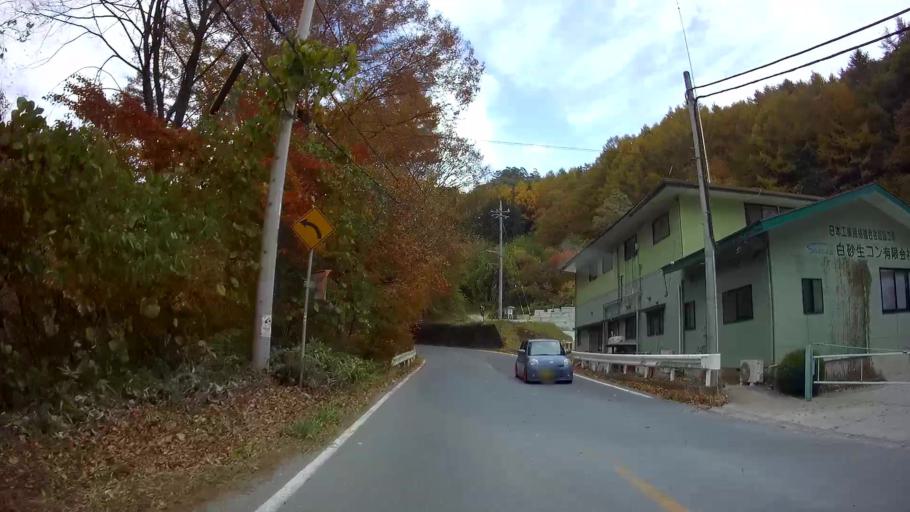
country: JP
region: Gunma
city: Nakanojomachi
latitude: 36.5594
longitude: 138.6406
